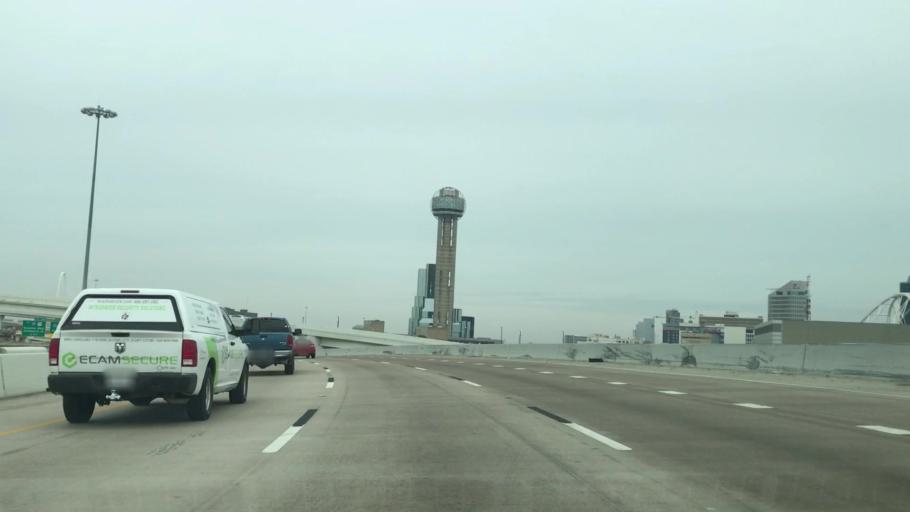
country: US
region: Texas
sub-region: Dallas County
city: Dallas
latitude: 32.7686
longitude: -96.8045
